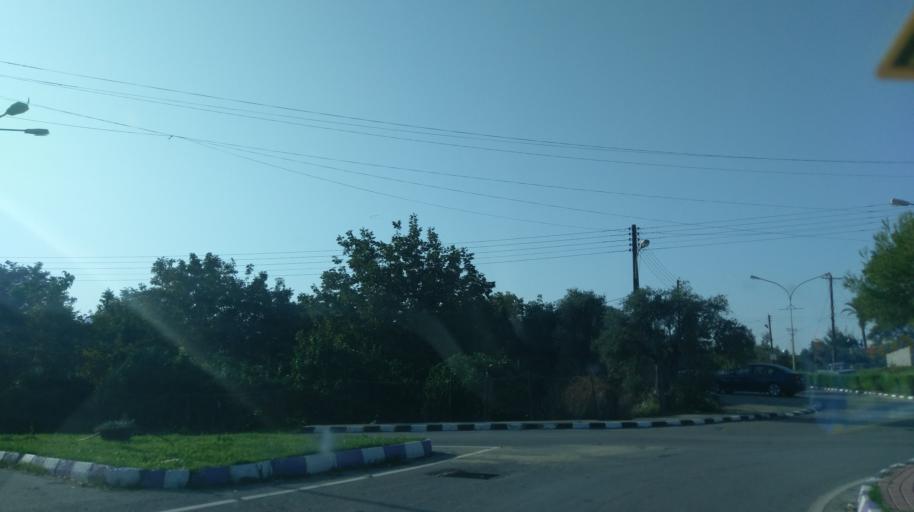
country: CY
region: Lefkosia
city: Lefka
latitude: 35.1177
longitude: 32.8503
